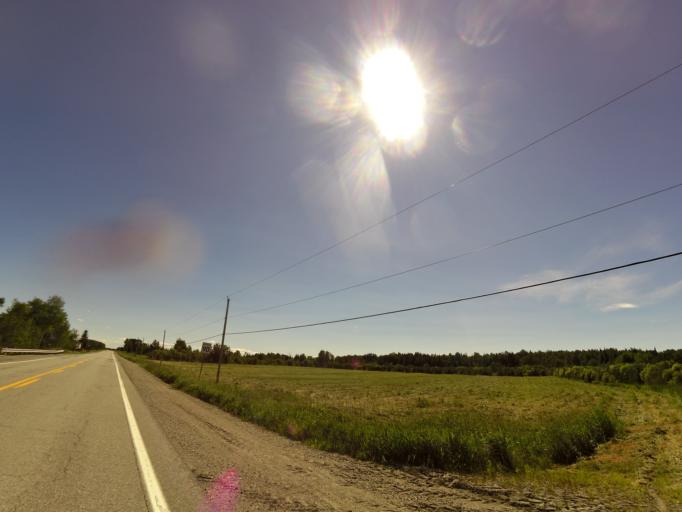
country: CA
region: Quebec
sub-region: Abitibi-Temiscamingue
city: Senneterre
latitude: 48.2650
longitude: -77.3258
